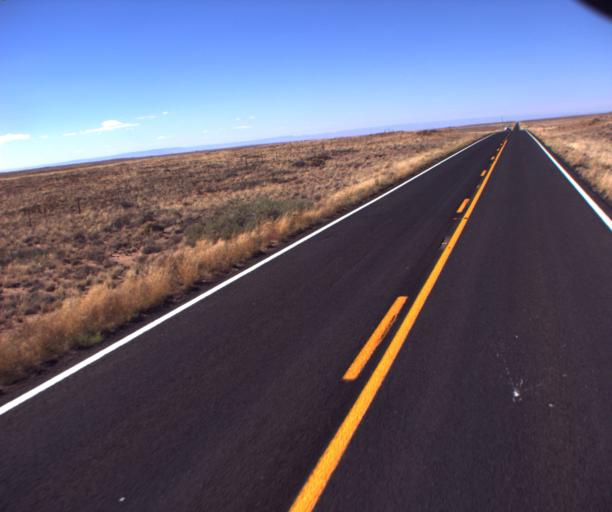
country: US
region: Arizona
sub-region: Coconino County
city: Tuba City
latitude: 35.9720
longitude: -110.9665
